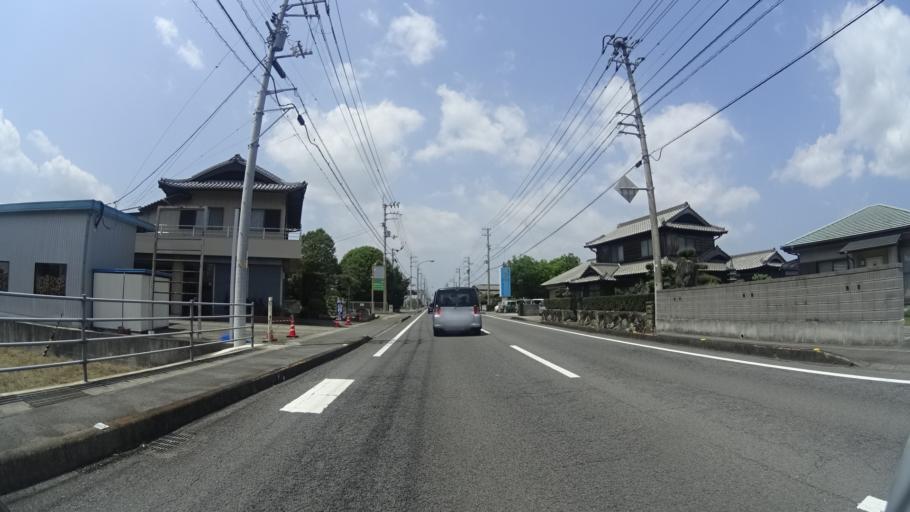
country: JP
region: Tokushima
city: Ishii
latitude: 34.0684
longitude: 134.4124
